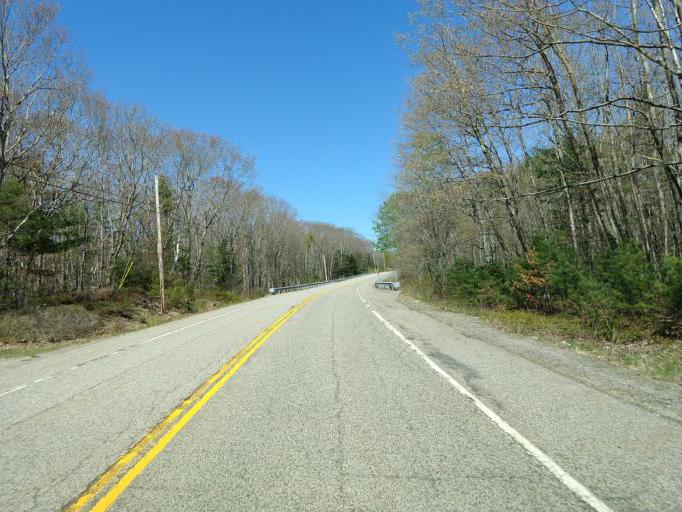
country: US
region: Maine
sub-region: York County
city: Arundel
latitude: 43.4226
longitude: -70.4057
